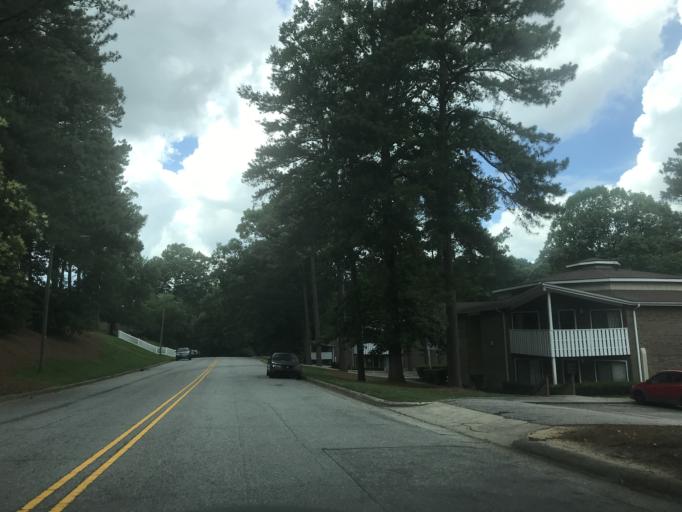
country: US
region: North Carolina
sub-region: Wake County
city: Raleigh
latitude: 35.8364
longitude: -78.6167
